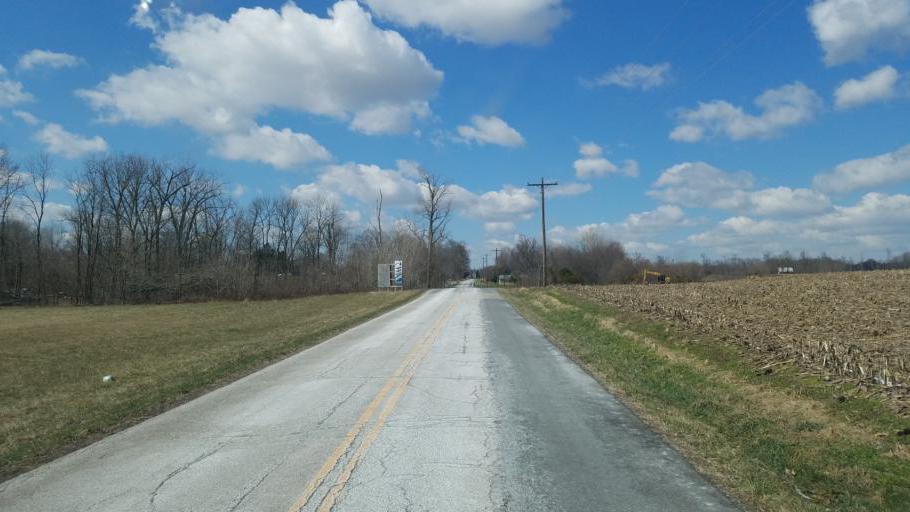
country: US
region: Ohio
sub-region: Knox County
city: Mount Vernon
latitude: 40.3144
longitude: -82.5531
